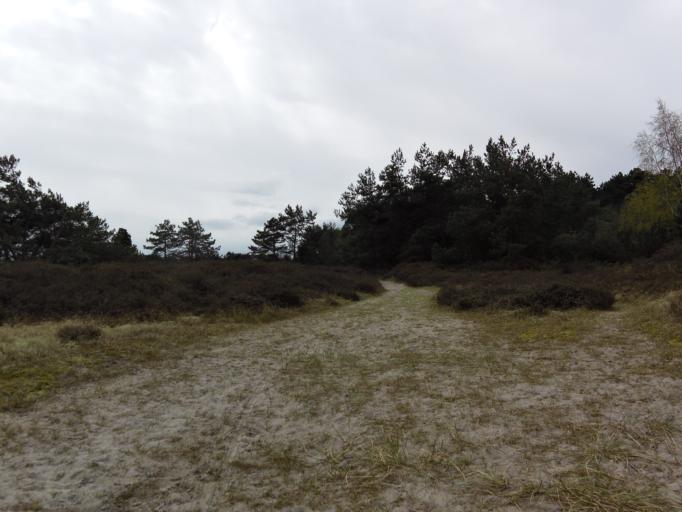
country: DE
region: Mecklenburg-Vorpommern
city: Hiddensee
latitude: 54.5412
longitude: 13.0913
